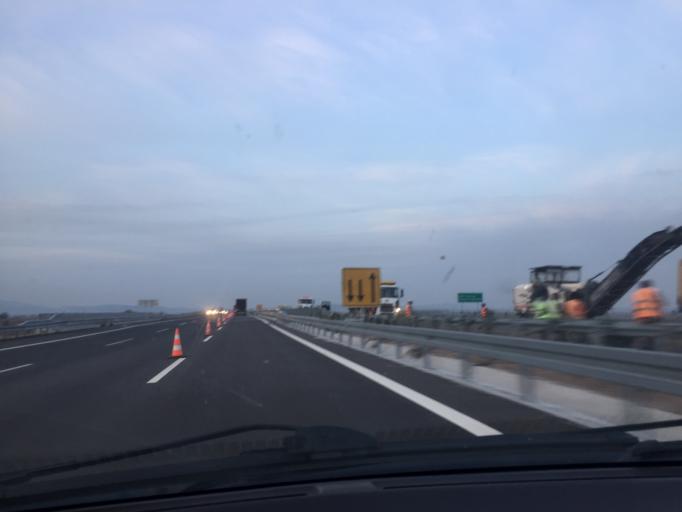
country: TR
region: Manisa
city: Halitpasa
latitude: 38.7235
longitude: 27.6527
